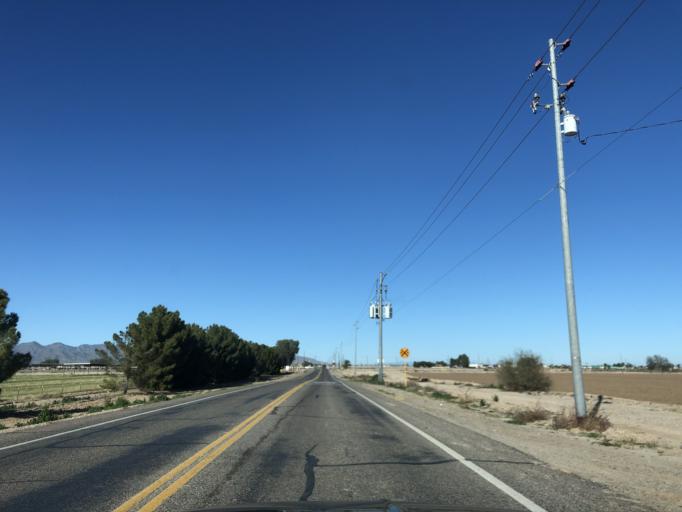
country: US
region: Arizona
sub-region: Maricopa County
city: Buckeye
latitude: 33.3925
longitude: -112.5042
